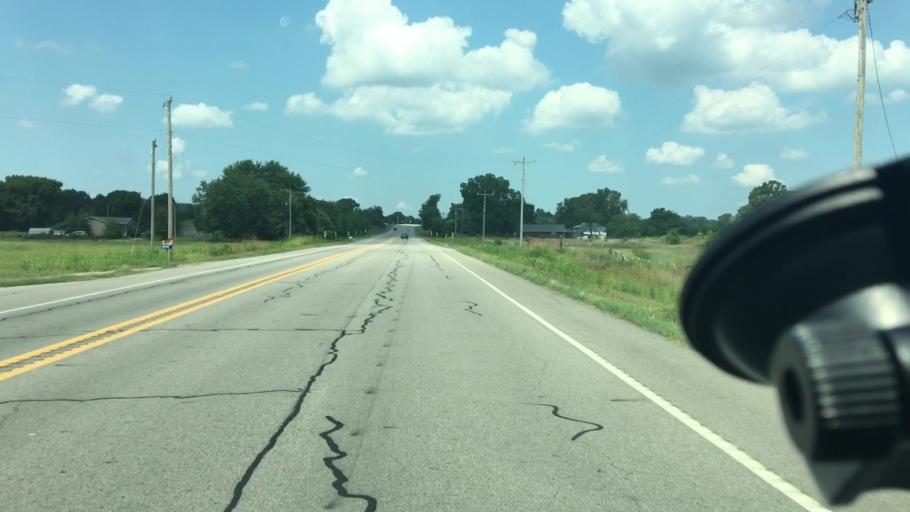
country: US
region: Arkansas
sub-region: Logan County
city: Paris
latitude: 35.2987
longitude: -93.8200
